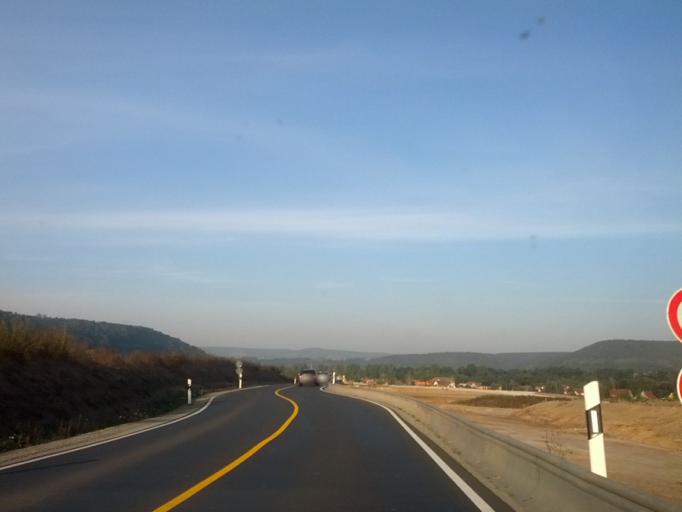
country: DE
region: Thuringia
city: Schops
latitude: 50.8294
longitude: 11.5905
